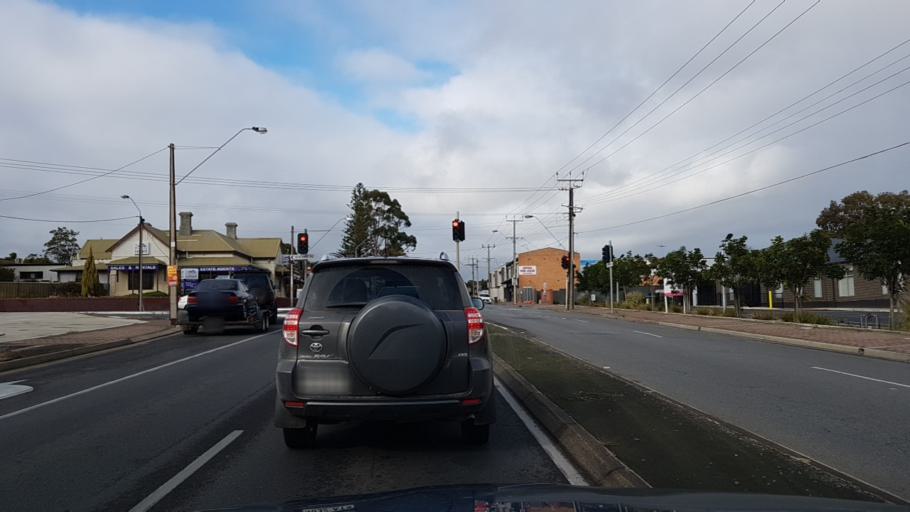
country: AU
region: South Australia
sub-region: Adelaide Hills
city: Seacliff
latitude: -35.0298
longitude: 138.5239
